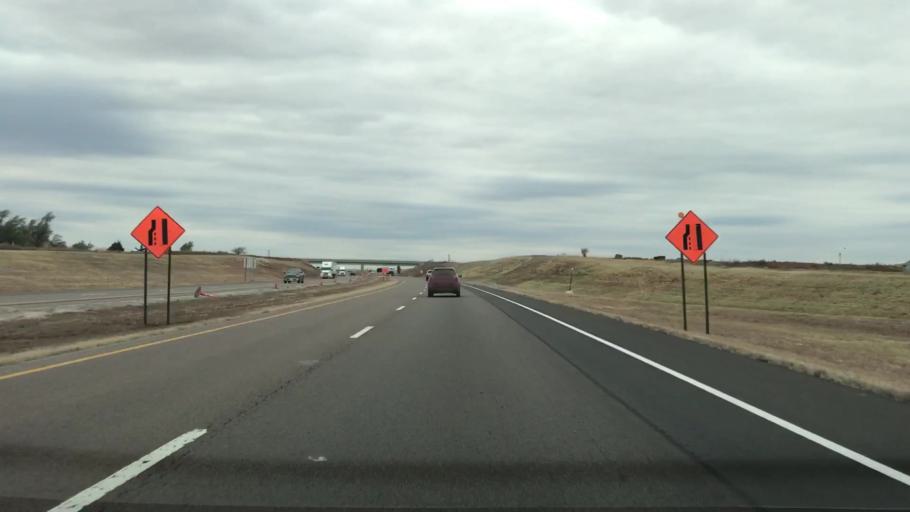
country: US
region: Oklahoma
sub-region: Beckham County
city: Elk City
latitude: 35.4262
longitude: -99.2784
